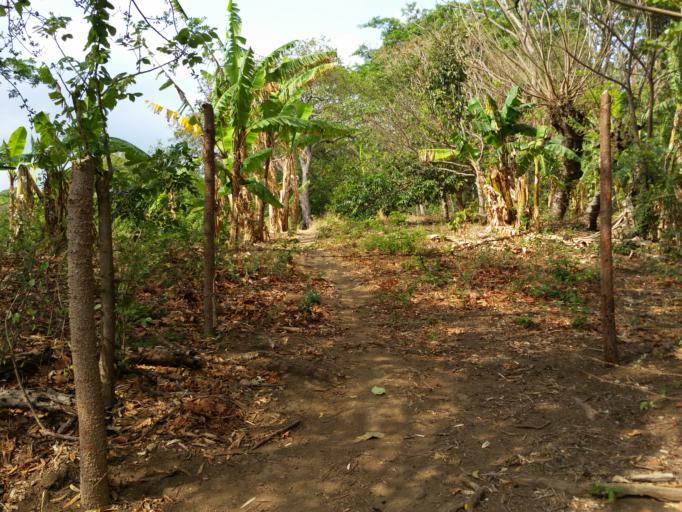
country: NI
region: Masaya
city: Ticuantepe
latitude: 12.0629
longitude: -86.2508
